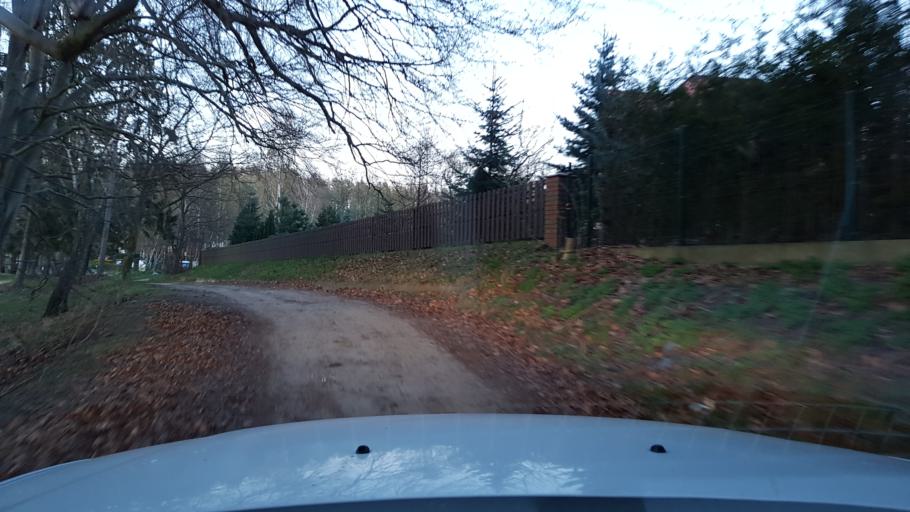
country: PL
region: West Pomeranian Voivodeship
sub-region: Powiat stargardzki
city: Insko
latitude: 53.4454
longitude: 15.5601
